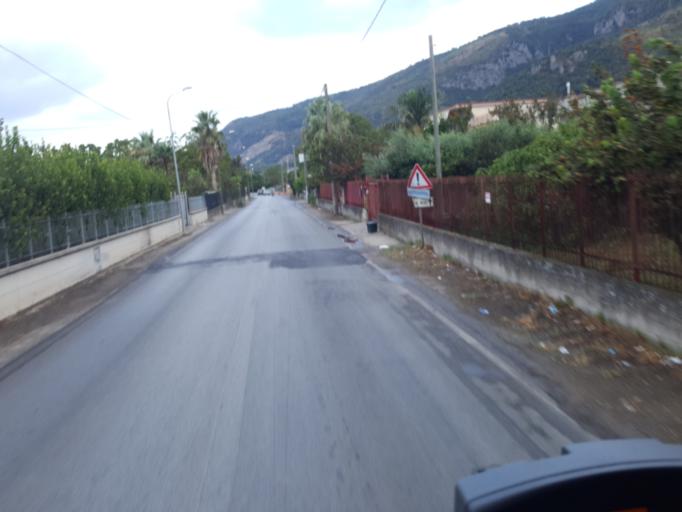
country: IT
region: Campania
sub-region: Provincia di Napoli
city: Striano
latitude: 40.8251
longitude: 14.5970
